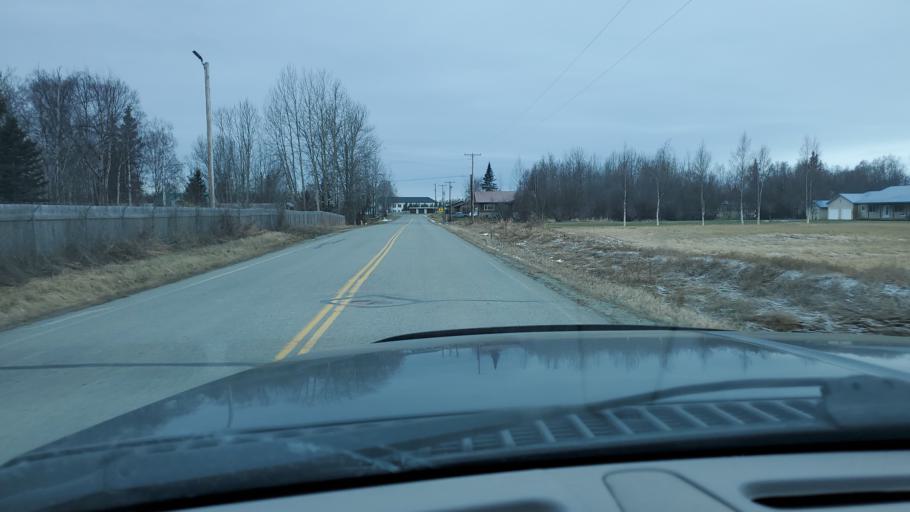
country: US
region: Alaska
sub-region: Matanuska-Susitna Borough
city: Palmer
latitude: 61.5994
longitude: -149.0979
